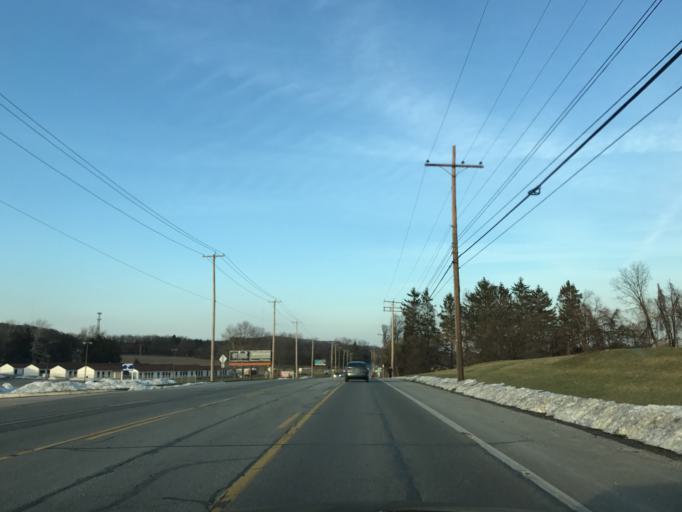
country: US
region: Pennsylvania
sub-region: York County
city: Stonybrook
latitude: 39.9931
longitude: -76.6353
